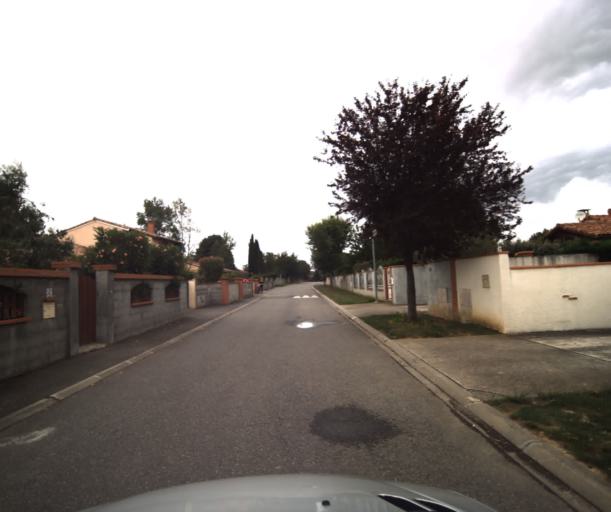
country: FR
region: Midi-Pyrenees
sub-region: Departement de la Haute-Garonne
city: Labarthe-sur-Leze
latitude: 43.4581
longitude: 1.4031
